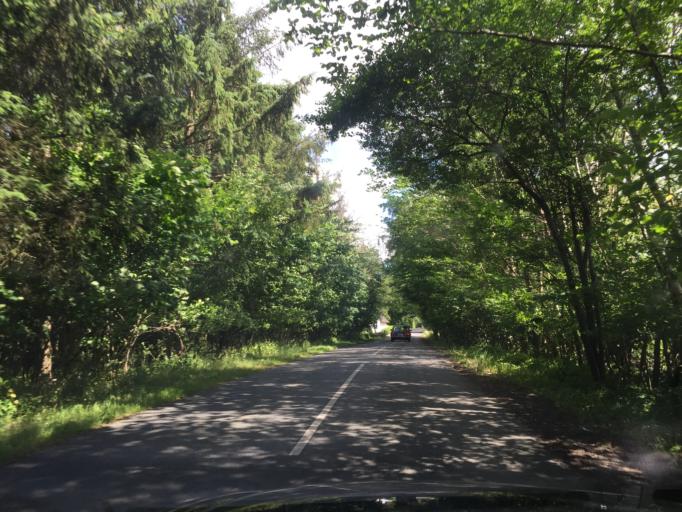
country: DK
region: Capital Region
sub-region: Egedal Kommune
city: Vekso
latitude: 55.7142
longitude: 12.2534
